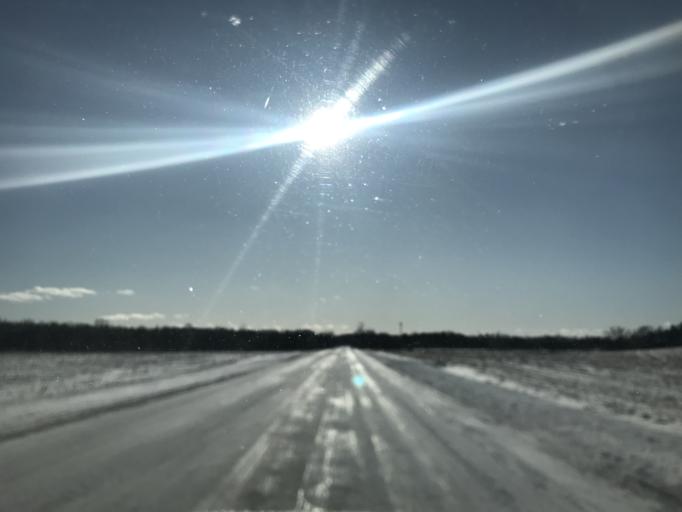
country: US
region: Wisconsin
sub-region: Door County
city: Sturgeon Bay
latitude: 44.8333
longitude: -87.5040
